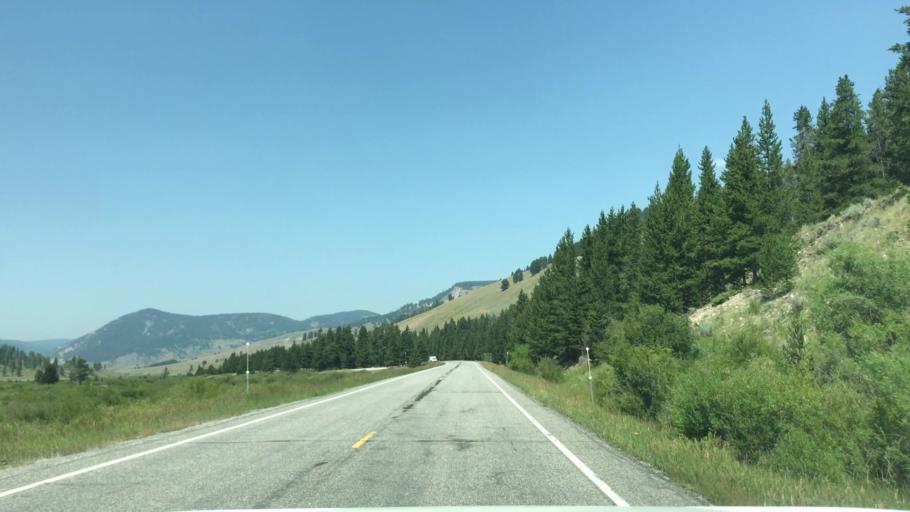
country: US
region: Montana
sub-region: Gallatin County
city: Big Sky
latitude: 45.0313
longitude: -111.1109
